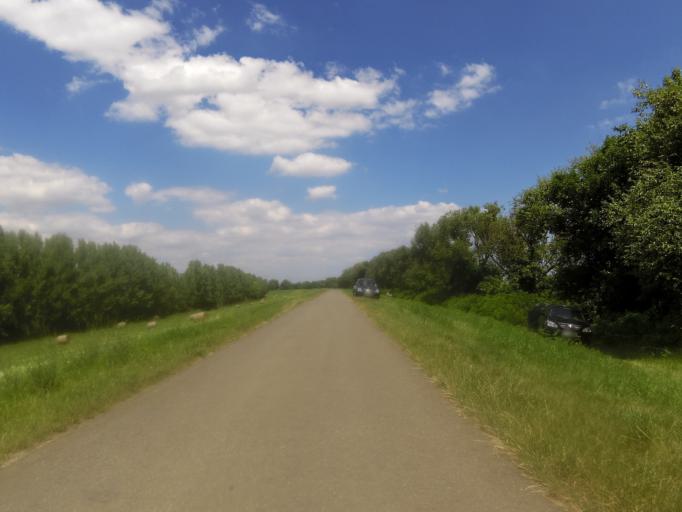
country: HU
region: Jasz-Nagykun-Szolnok
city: Abadszalok
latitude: 47.5331
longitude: 20.6023
